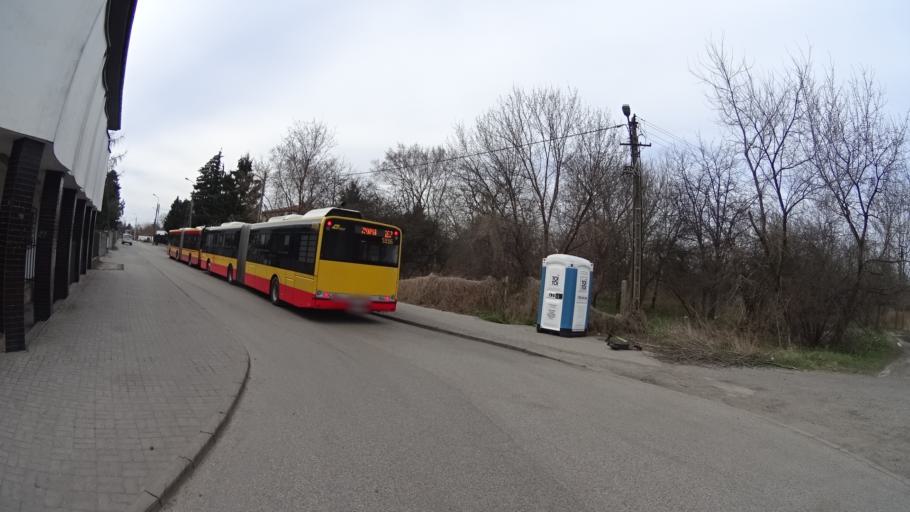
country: PL
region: Masovian Voivodeship
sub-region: Warszawa
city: Praga Poludnie
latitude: 52.2081
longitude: 21.0836
